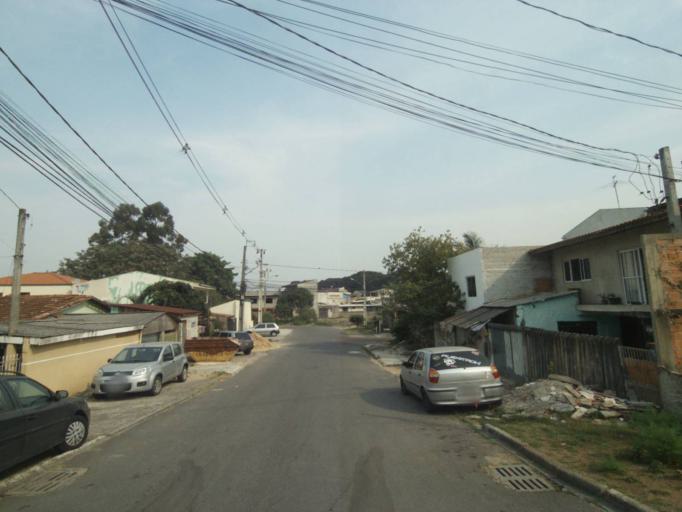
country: BR
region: Parana
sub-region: Sao Jose Dos Pinhais
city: Sao Jose dos Pinhais
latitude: -25.5221
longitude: -49.2748
